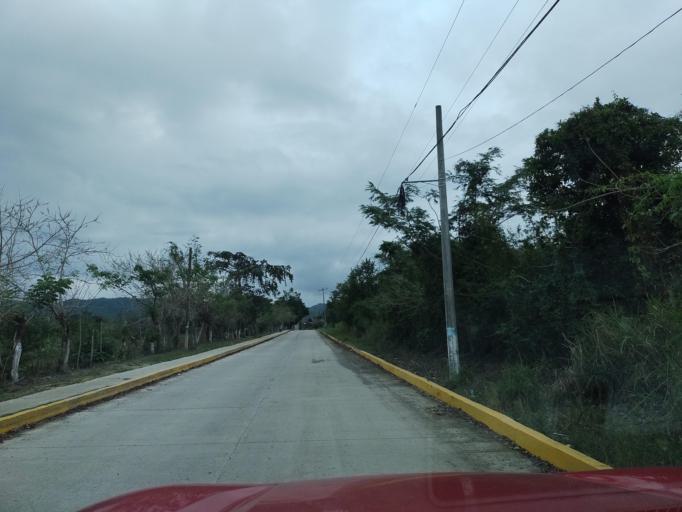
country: MX
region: Veracruz
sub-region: Papantla
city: El Chote
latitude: 20.4336
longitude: -97.3802
